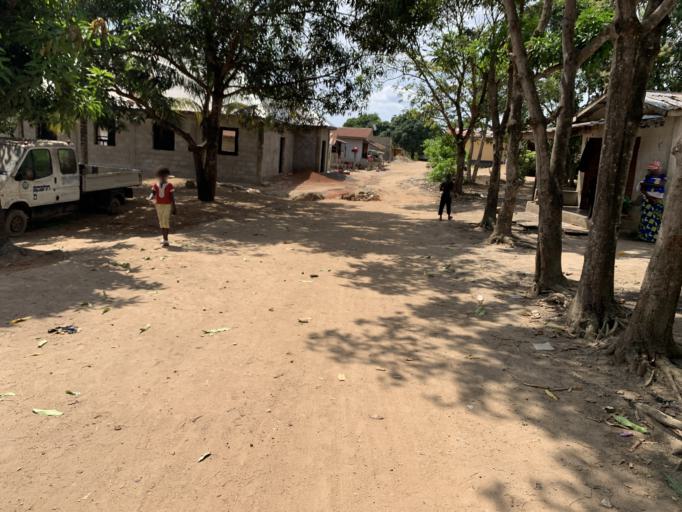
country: SL
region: Western Area
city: Waterloo
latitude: 8.3292
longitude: -13.0459
